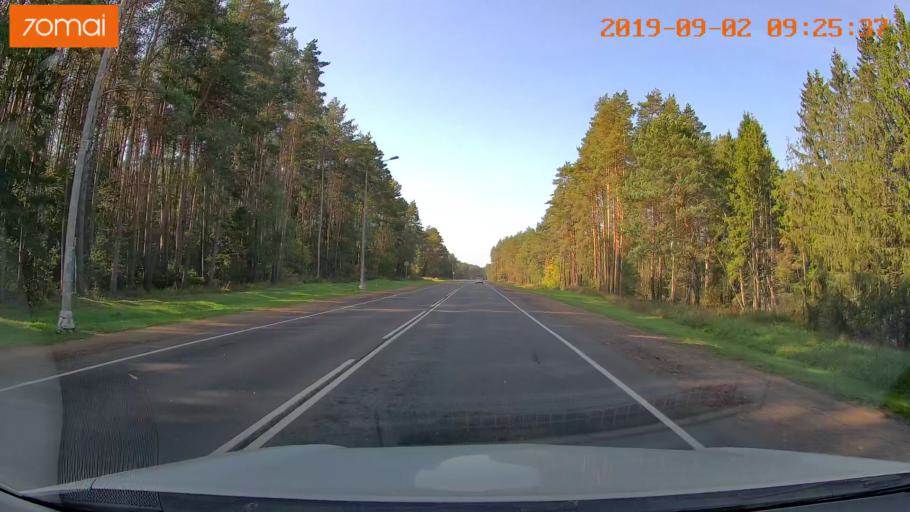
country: RU
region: Kaluga
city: Yukhnov
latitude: 54.7567
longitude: 35.2744
